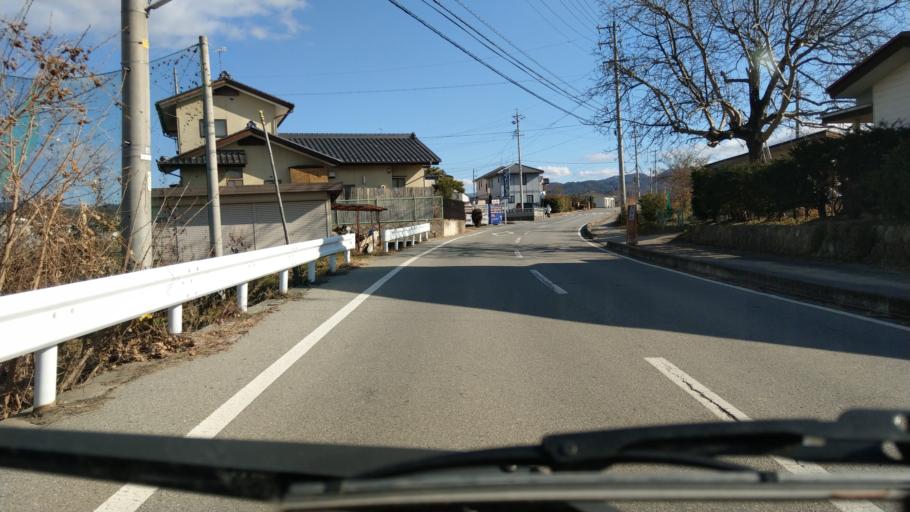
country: JP
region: Nagano
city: Saku
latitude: 36.2457
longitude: 138.4616
